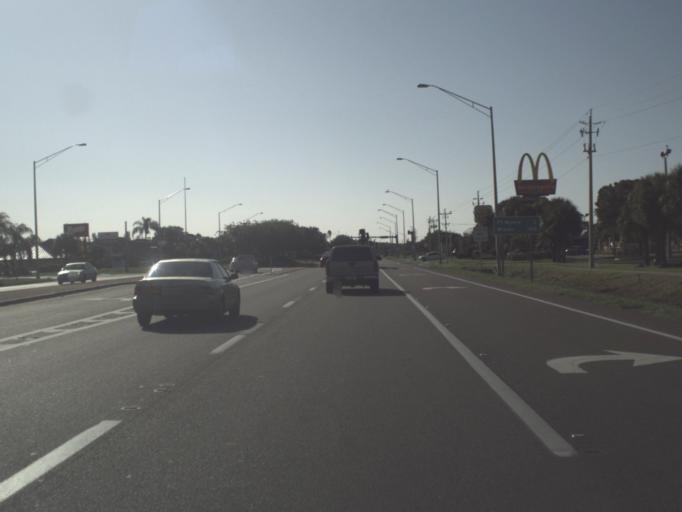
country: US
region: Florida
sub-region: Lee County
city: North Fort Myers
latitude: 26.6659
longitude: -81.8888
